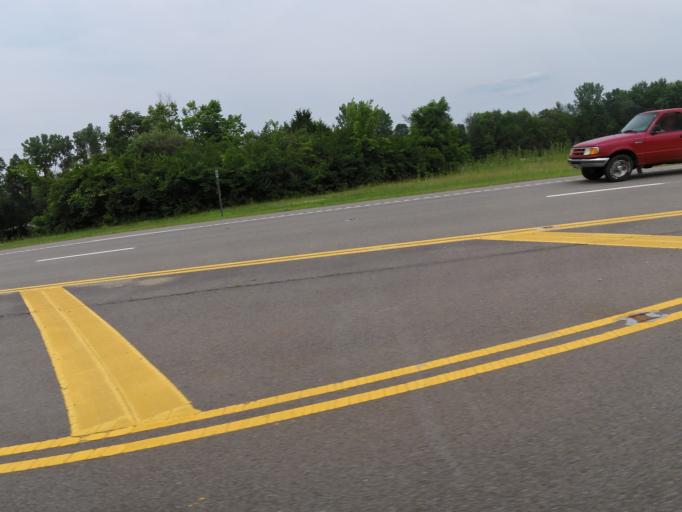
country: US
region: Ohio
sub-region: Warren County
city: Waynesville
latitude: 39.4995
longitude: -83.9963
